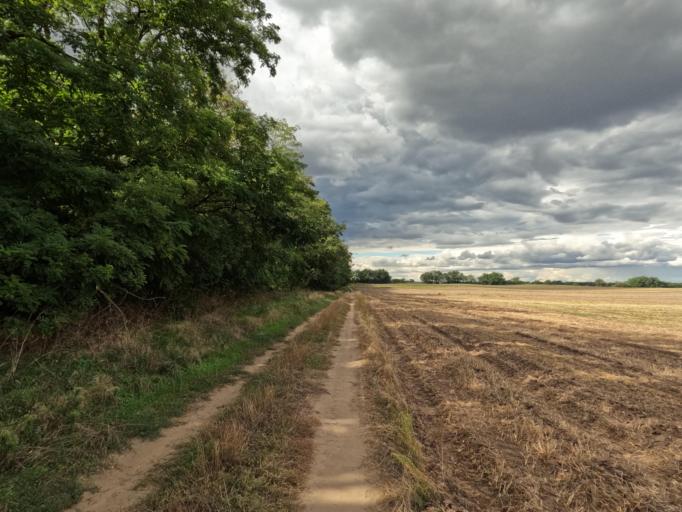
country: HU
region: Tolna
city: Tengelic
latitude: 46.5199
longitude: 18.6774
